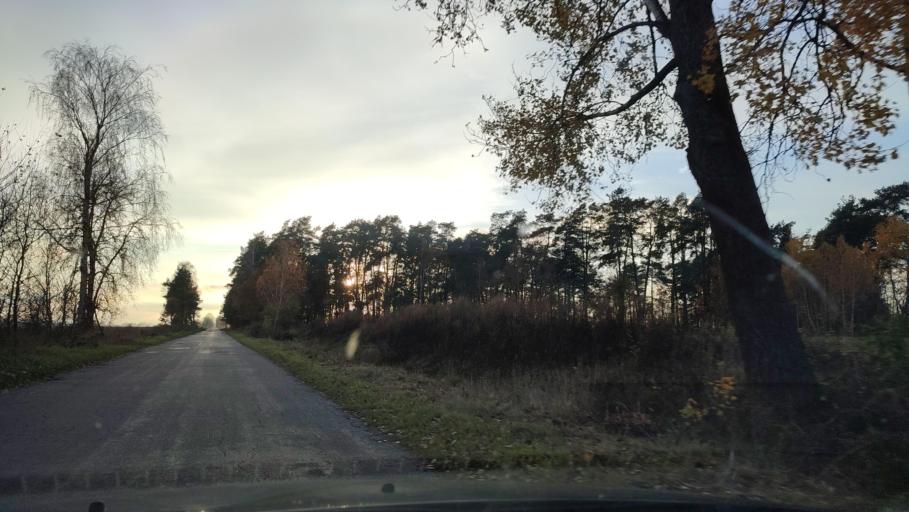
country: PL
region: Masovian Voivodeship
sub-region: Powiat mlawski
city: Dzierzgowo
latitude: 53.2553
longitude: 20.5966
